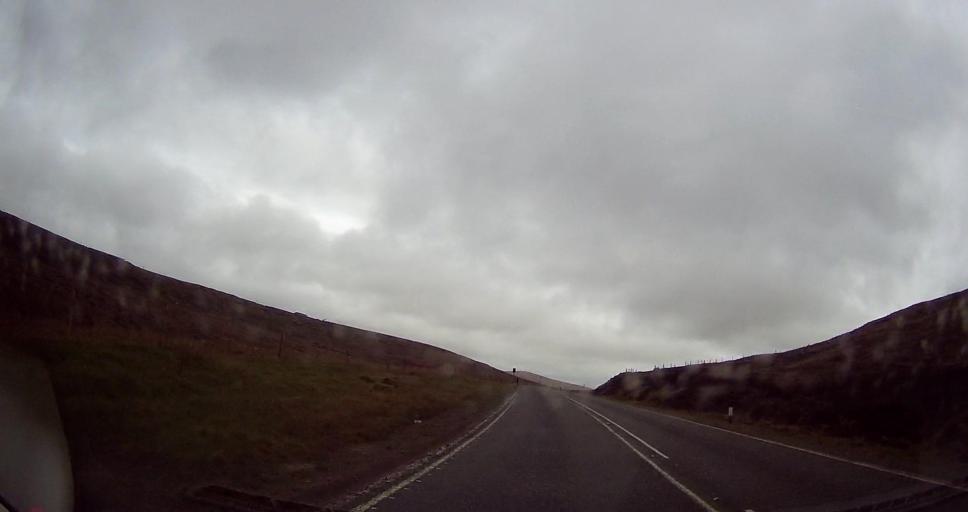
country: GB
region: Scotland
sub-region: Shetland Islands
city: Lerwick
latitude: 60.3208
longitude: -1.2494
